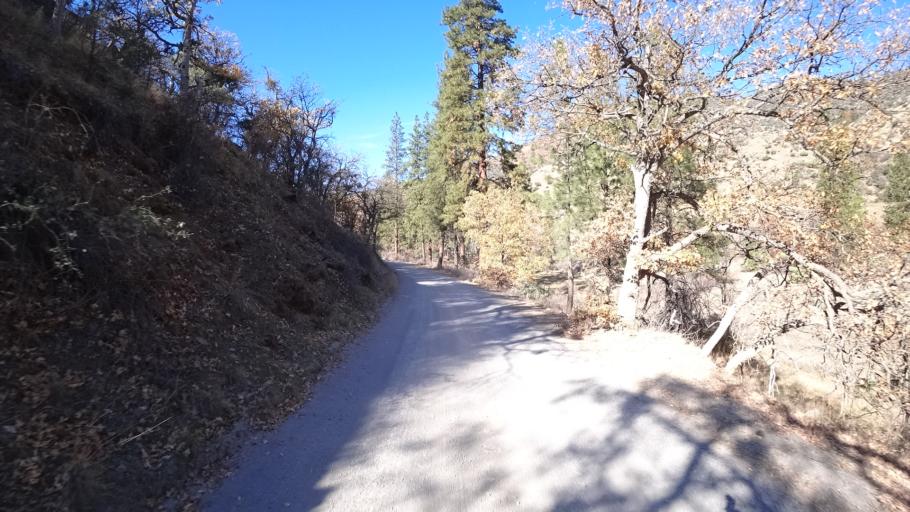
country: US
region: California
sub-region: Siskiyou County
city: Yreka
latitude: 41.8293
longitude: -122.6517
